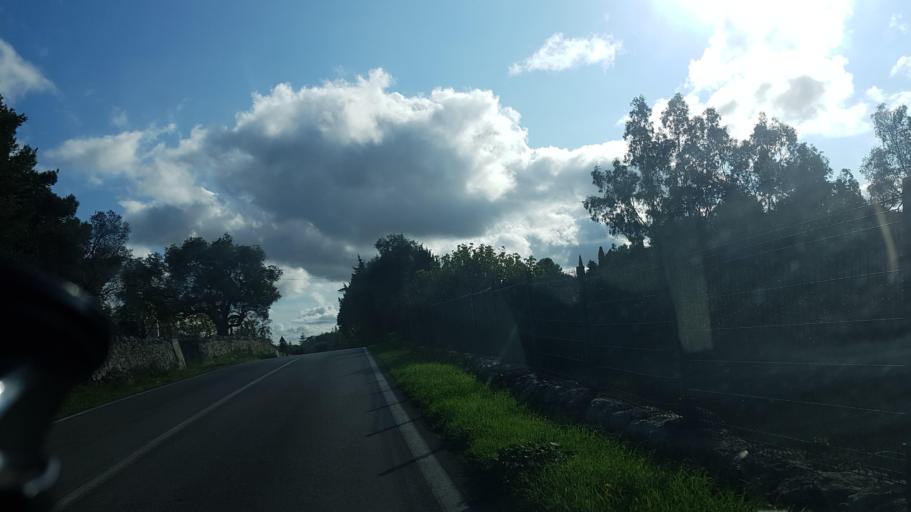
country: IT
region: Apulia
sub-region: Provincia di Brindisi
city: Ostuni
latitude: 40.6954
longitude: 17.5875
